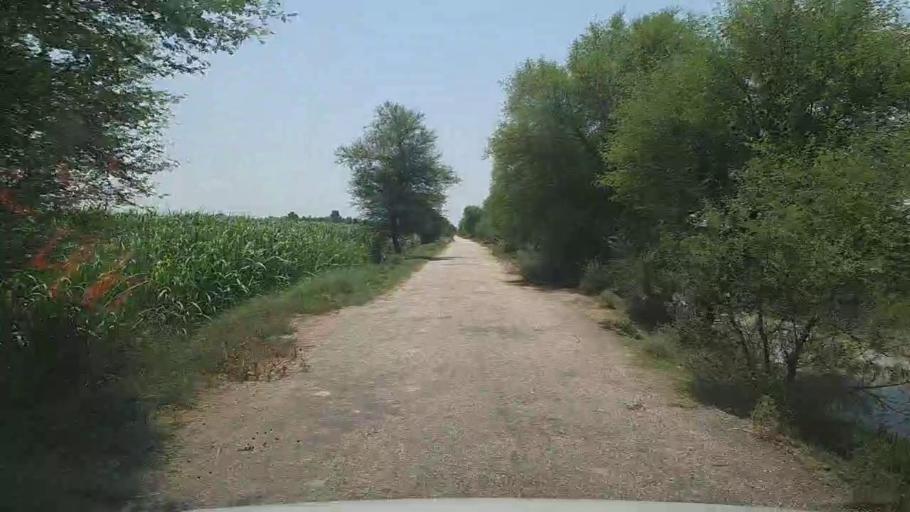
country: PK
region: Sindh
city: Ubauro
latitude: 28.1601
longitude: 69.7452
